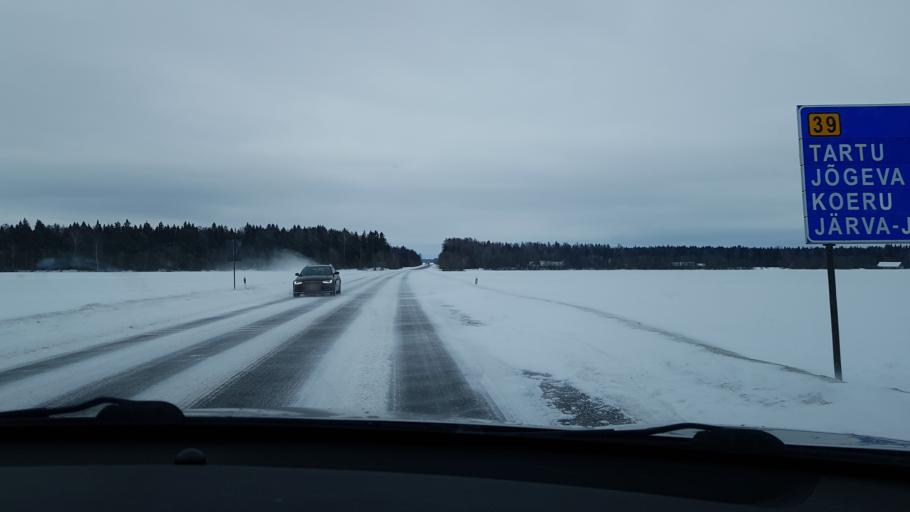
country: EE
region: Jaervamaa
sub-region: Jaerva-Jaani vald
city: Jarva-Jaani
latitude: 59.1386
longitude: 25.7711
